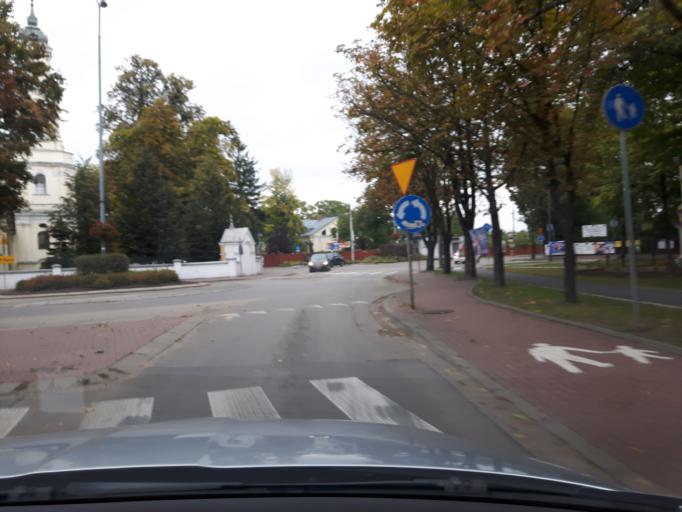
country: PL
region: Masovian Voivodeship
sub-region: Powiat wolominski
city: Kobylka
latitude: 52.3391
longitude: 21.1960
